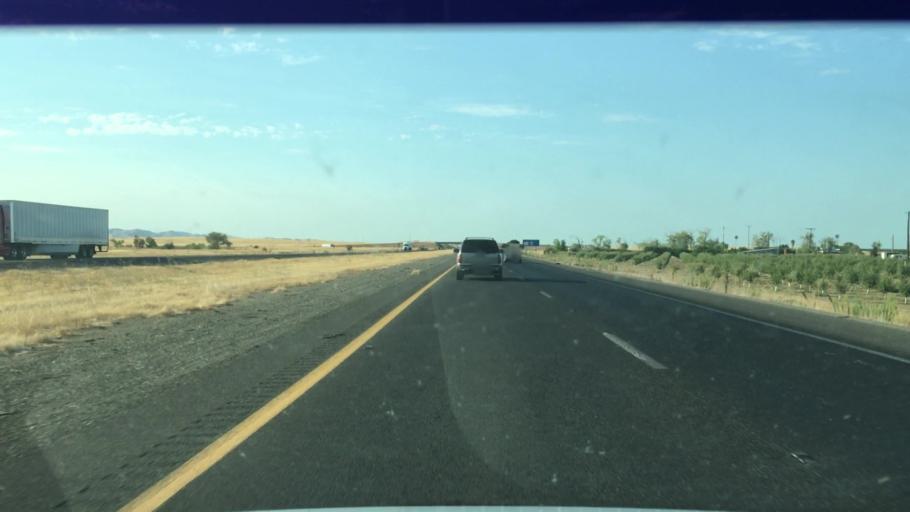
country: US
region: California
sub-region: Merced County
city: Gustine
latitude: 37.2367
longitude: -121.0864
